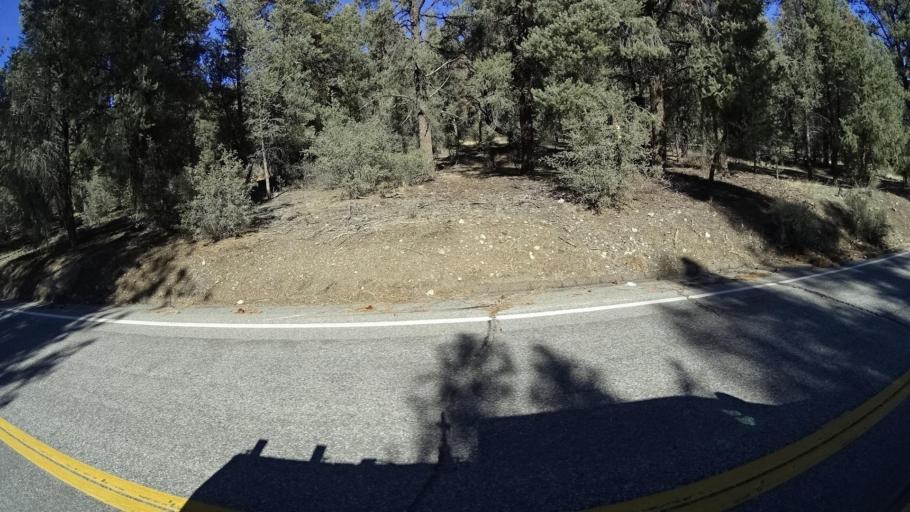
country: US
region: California
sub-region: Kern County
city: Pine Mountain Club
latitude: 34.8542
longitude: -119.1841
